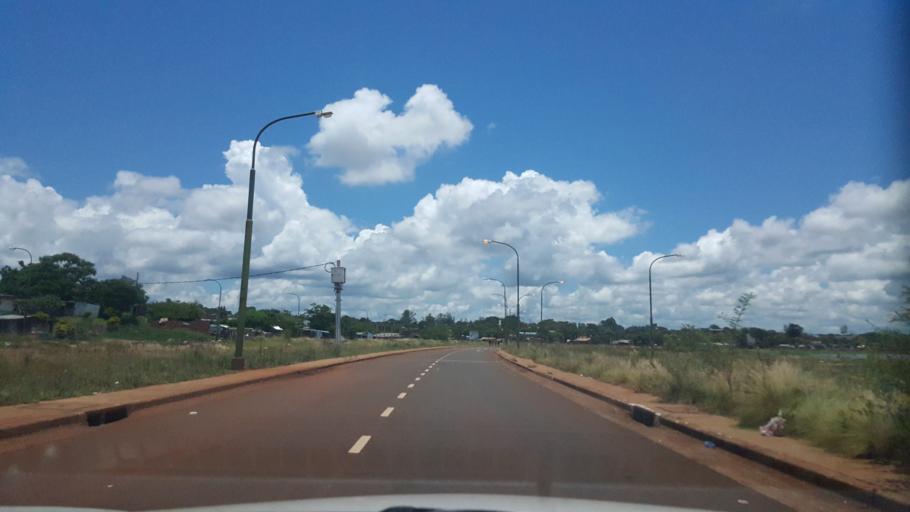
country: AR
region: Misiones
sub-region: Departamento de Capital
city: Posadas
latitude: -27.4195
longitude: -55.8882
